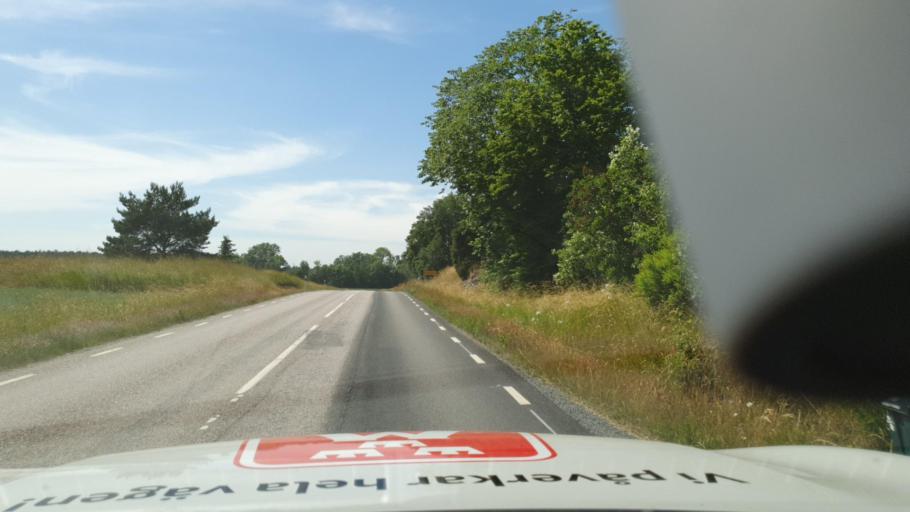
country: SE
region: Vaestra Goetaland
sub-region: Vara Kommun
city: Vara
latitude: 58.4805
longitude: 12.8718
